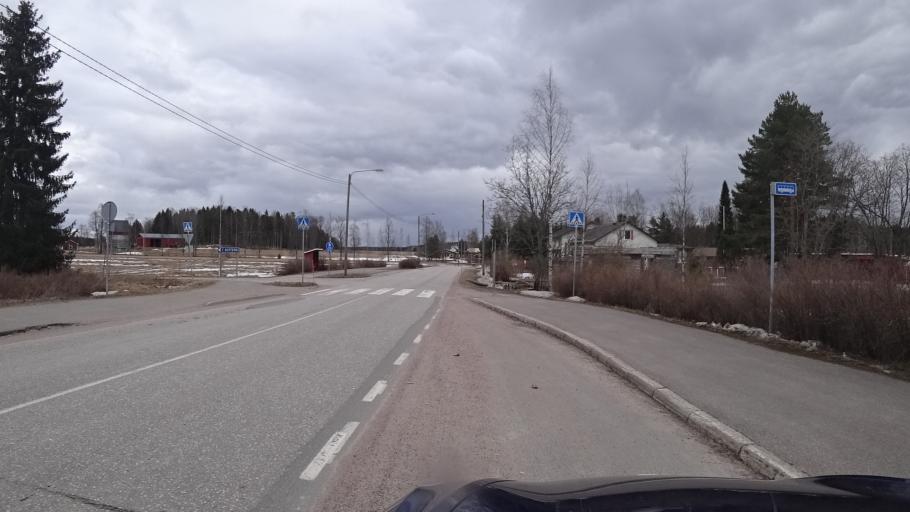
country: FI
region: Paijanne Tavastia
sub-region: Lahti
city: Nastola
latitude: 60.8724
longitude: 26.0078
